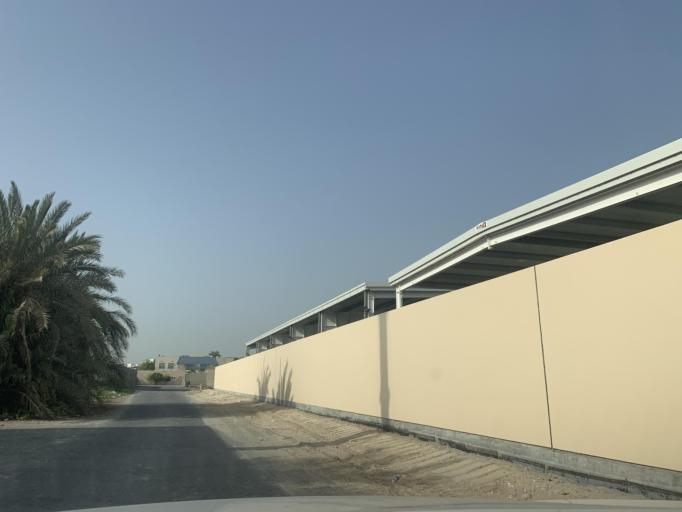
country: BH
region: Central Governorate
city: Madinat Hamad
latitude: 26.1568
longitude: 50.4910
